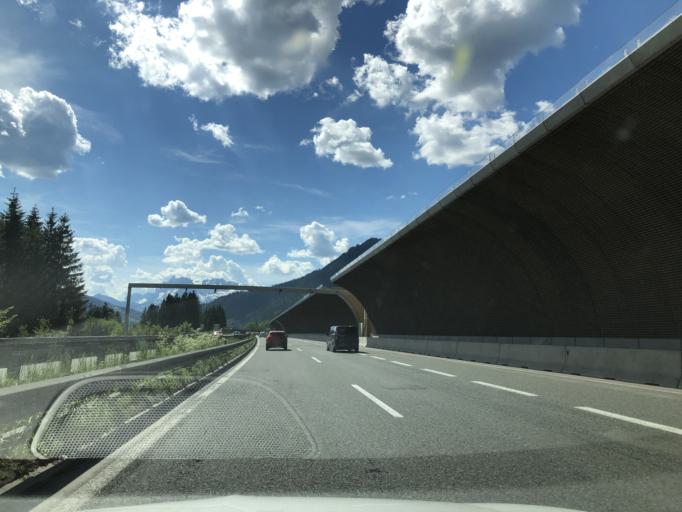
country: AT
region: Salzburg
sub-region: Politischer Bezirk Sankt Johann im Pongau
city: Eben im Pongau
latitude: 47.4228
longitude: 13.3749
